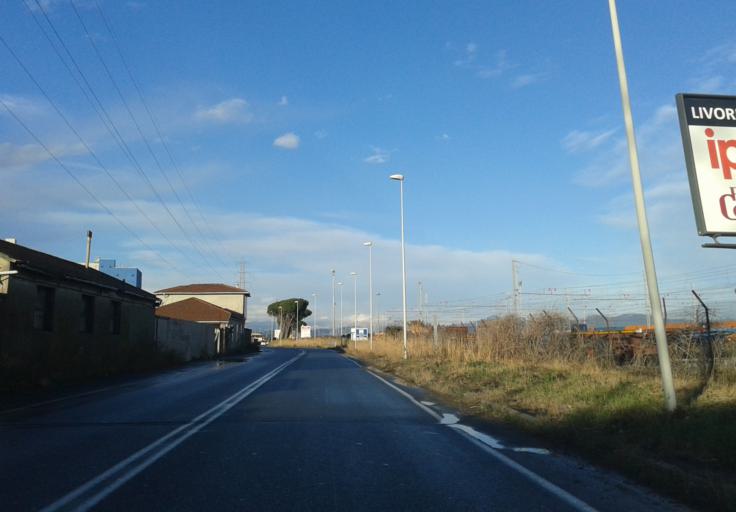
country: IT
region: Tuscany
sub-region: Provincia di Livorno
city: Livorno
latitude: 43.5753
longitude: 10.3207
